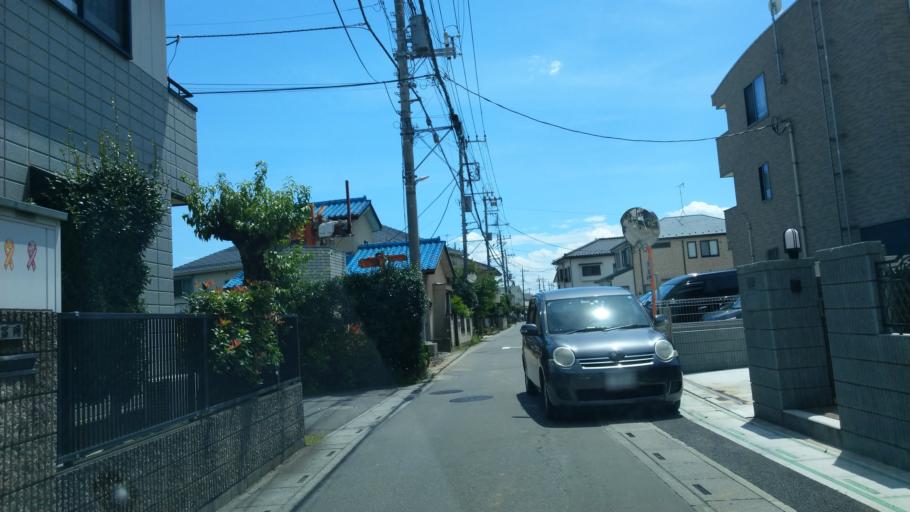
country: JP
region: Saitama
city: Ageoshimo
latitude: 35.9223
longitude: 139.5831
